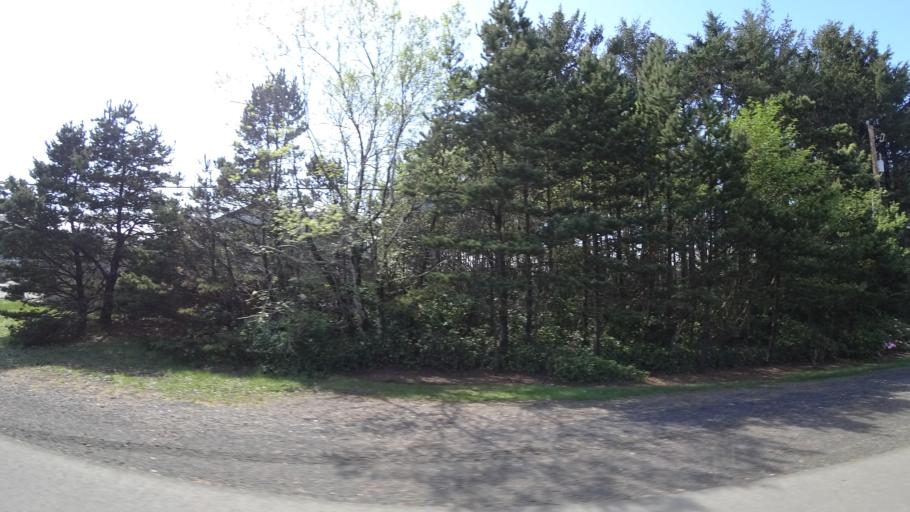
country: US
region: Oregon
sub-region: Lincoln County
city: Newport
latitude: 44.6911
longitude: -124.0634
